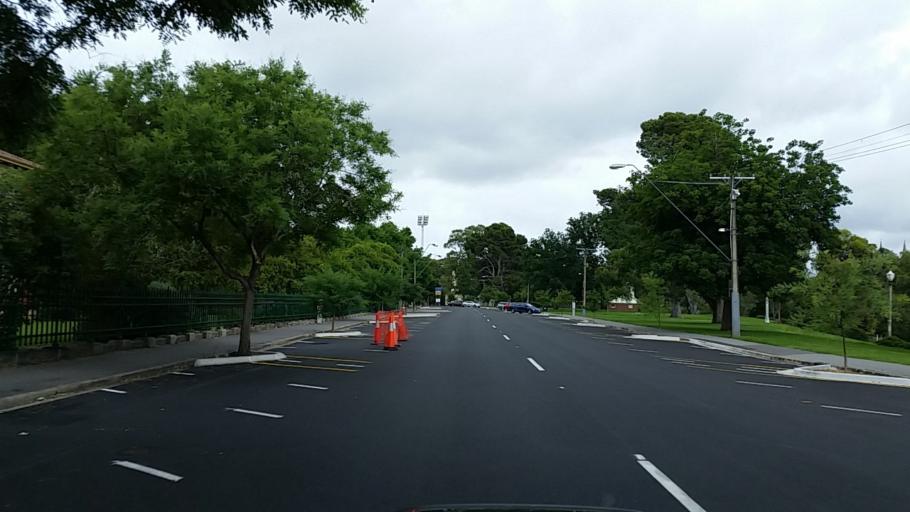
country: AU
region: South Australia
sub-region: Adelaide
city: Adelaide
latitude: -34.9177
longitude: 138.6029
